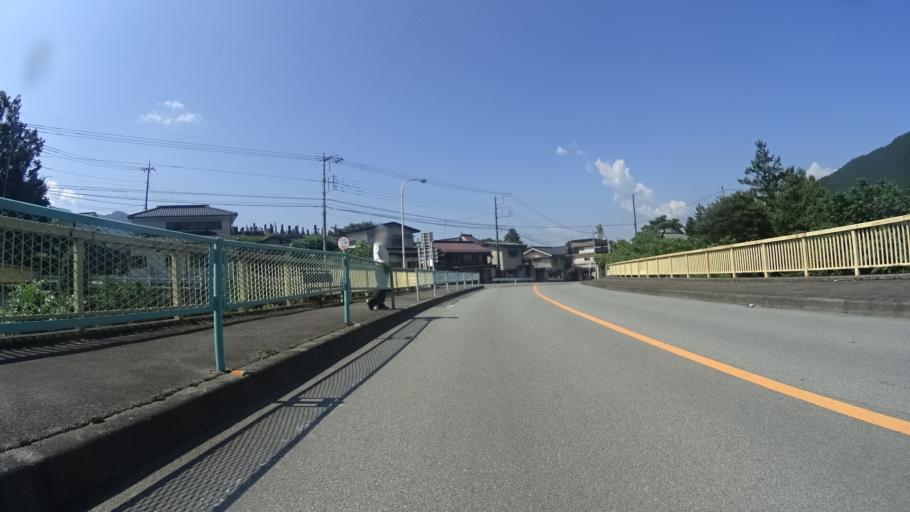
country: JP
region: Yamanashi
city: Enzan
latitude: 35.7287
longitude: 138.7694
